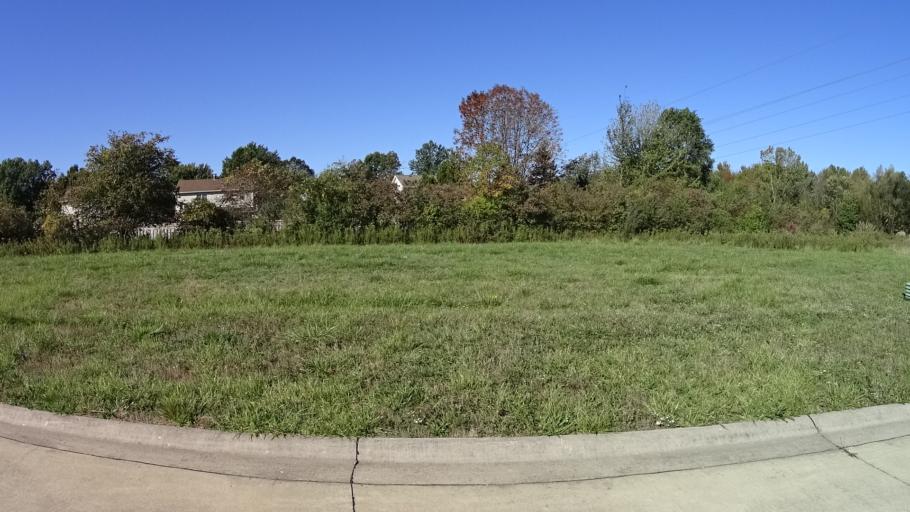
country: US
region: Ohio
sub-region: Lorain County
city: Amherst
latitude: 41.4236
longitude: -82.2181
